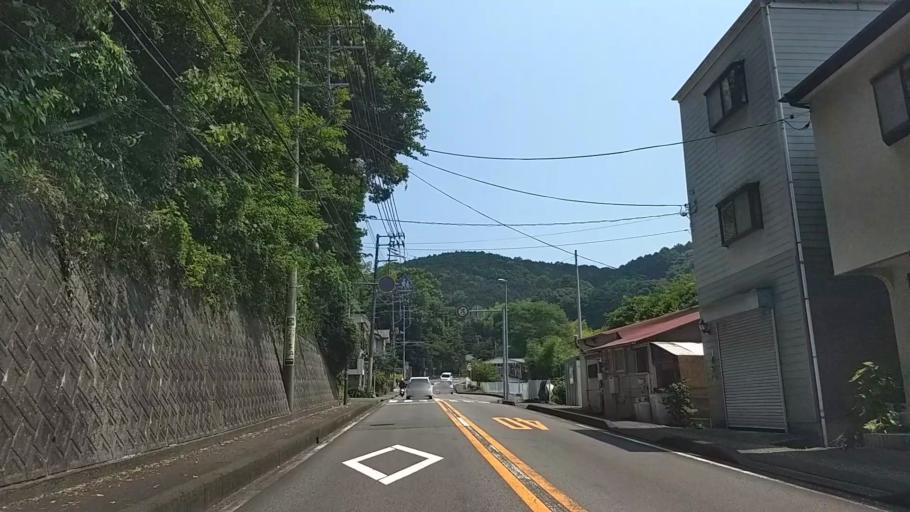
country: JP
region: Shizuoka
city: Ito
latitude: 34.9614
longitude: 139.1038
